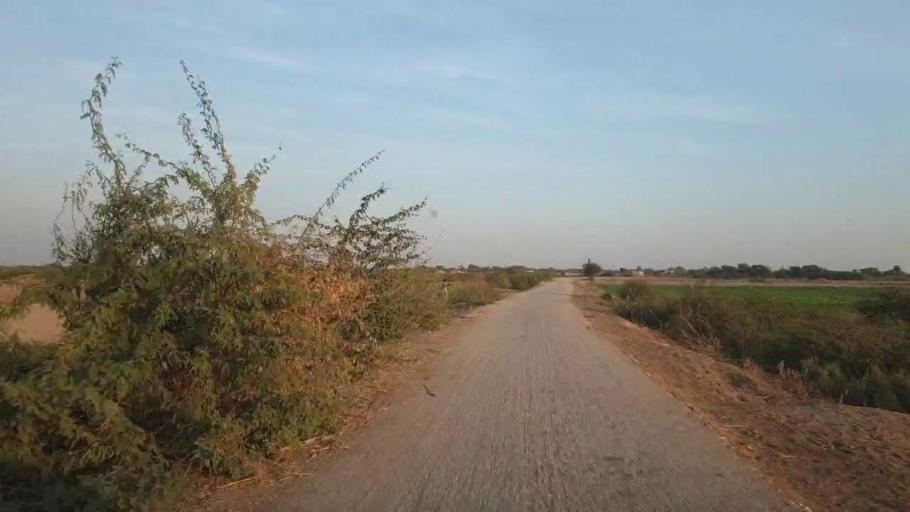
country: PK
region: Sindh
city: Chambar
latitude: 25.2826
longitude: 68.8285
